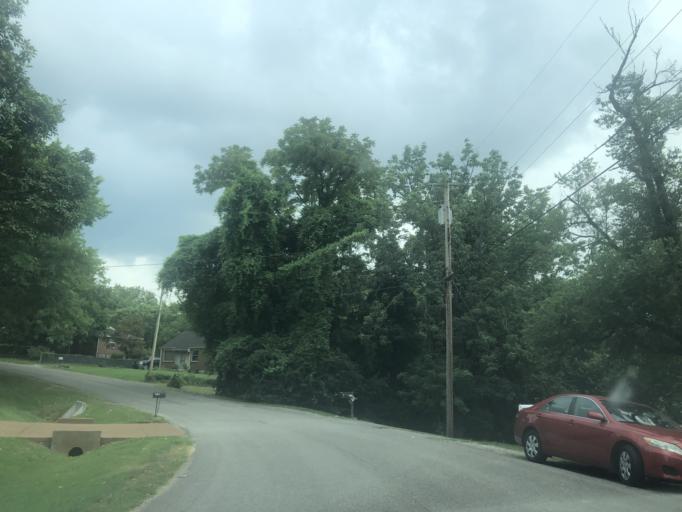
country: US
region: Tennessee
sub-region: Davidson County
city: Nashville
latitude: 36.1556
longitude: -86.6866
